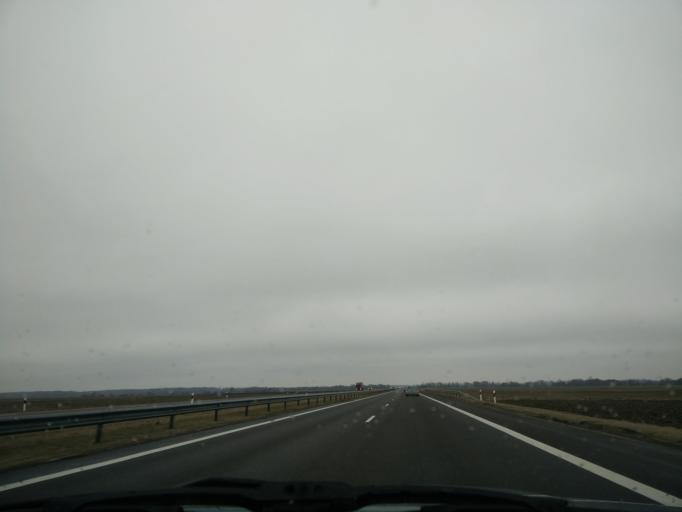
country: LT
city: Raseiniai
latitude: 55.3606
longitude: 23.0156
